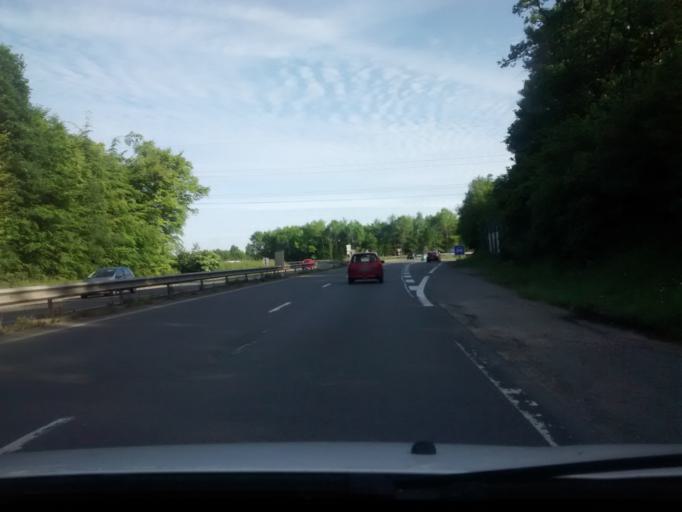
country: FR
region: Brittany
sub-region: Departement d'Ille-et-Vilaine
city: Cesson-Sevigne
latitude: 48.1389
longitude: -1.6273
